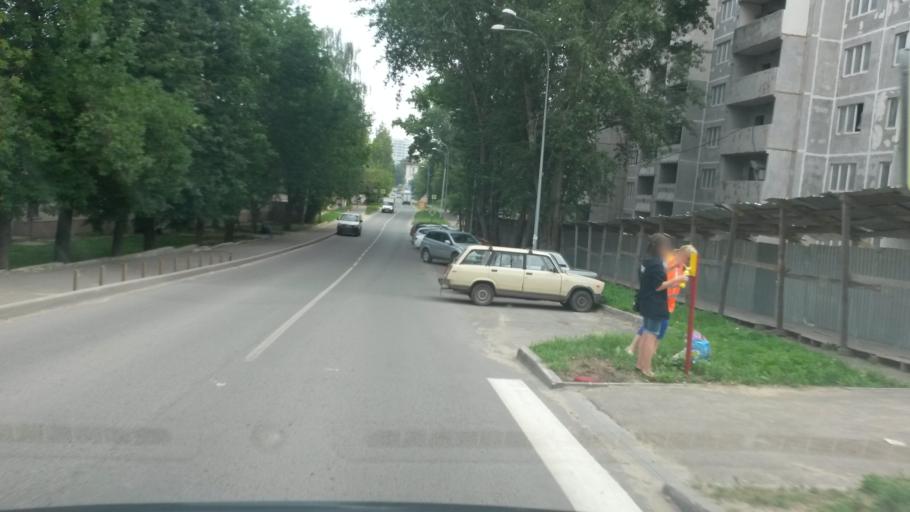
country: RU
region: Ivanovo
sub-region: Gorod Ivanovo
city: Ivanovo
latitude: 57.0053
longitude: 40.9622
